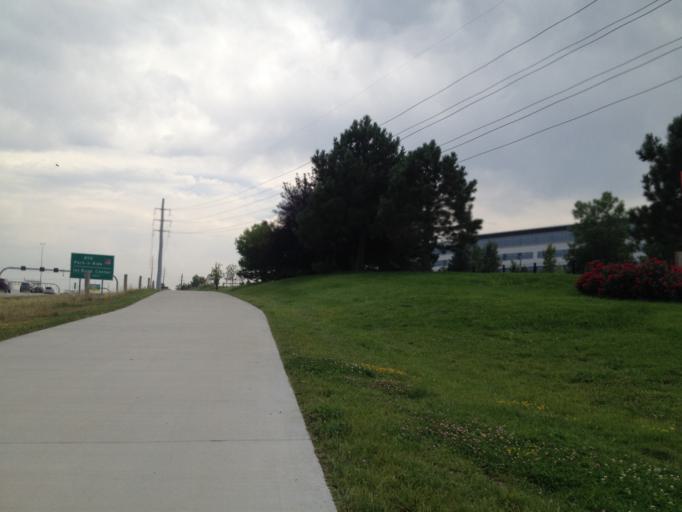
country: US
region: Colorado
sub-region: Broomfield County
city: Broomfield
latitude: 39.9212
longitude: -105.1055
